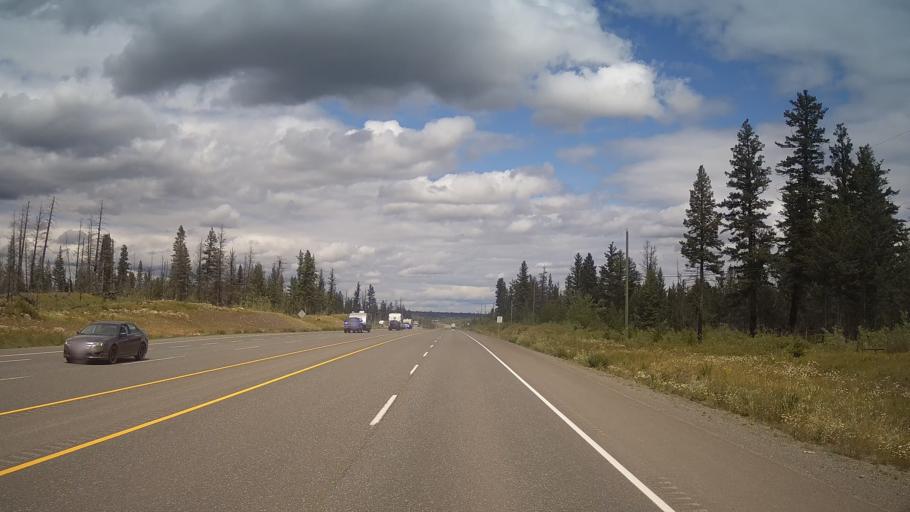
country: CA
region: British Columbia
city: Cache Creek
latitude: 51.3293
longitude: -121.3846
